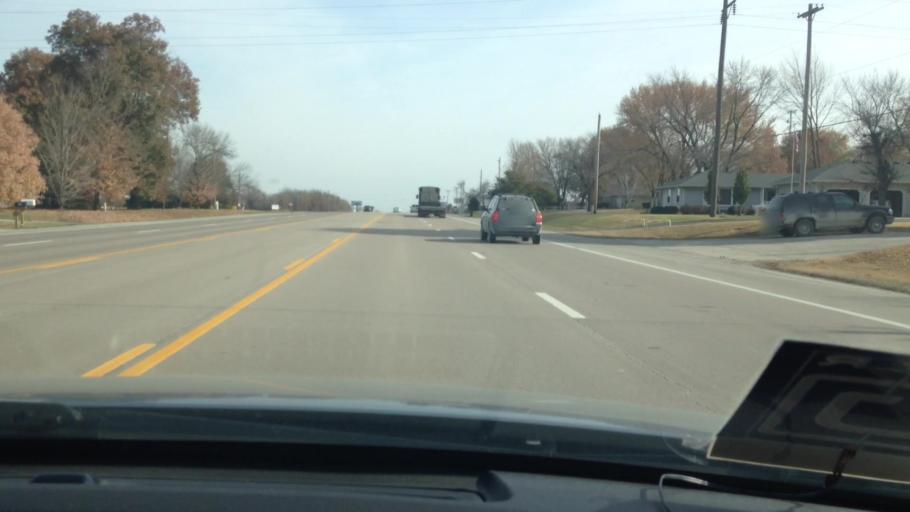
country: US
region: Missouri
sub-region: Henry County
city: Clinton
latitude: 38.3895
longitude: -93.8071
